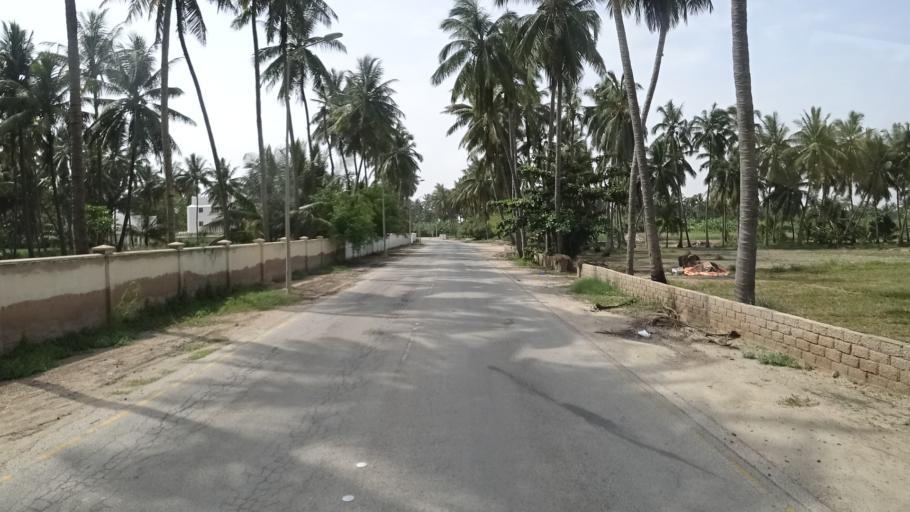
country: OM
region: Zufar
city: Salalah
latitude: 17.0136
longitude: 54.1529
